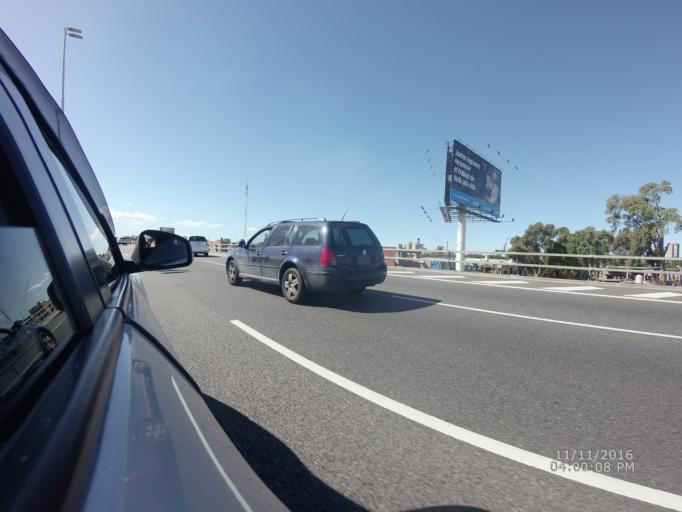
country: AR
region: Buenos Aires F.D.
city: Retiro
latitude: -34.5833
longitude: -58.3805
